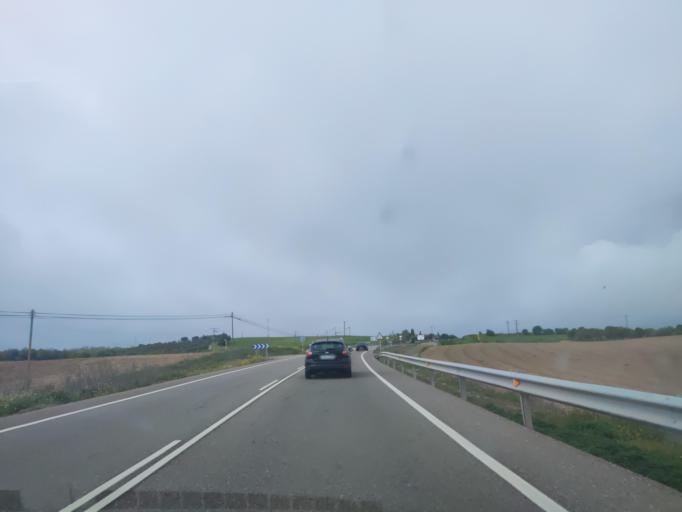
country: ES
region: Castille-La Mancha
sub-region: Province of Toledo
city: Olias del Rey
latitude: 39.9437
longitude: -4.0024
